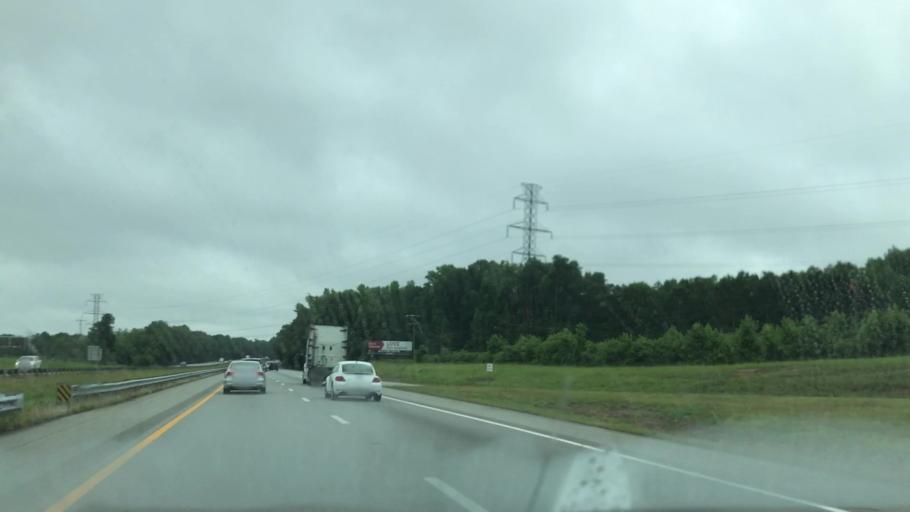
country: US
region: North Carolina
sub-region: Halifax County
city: Halifax
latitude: 36.3651
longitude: -77.6717
